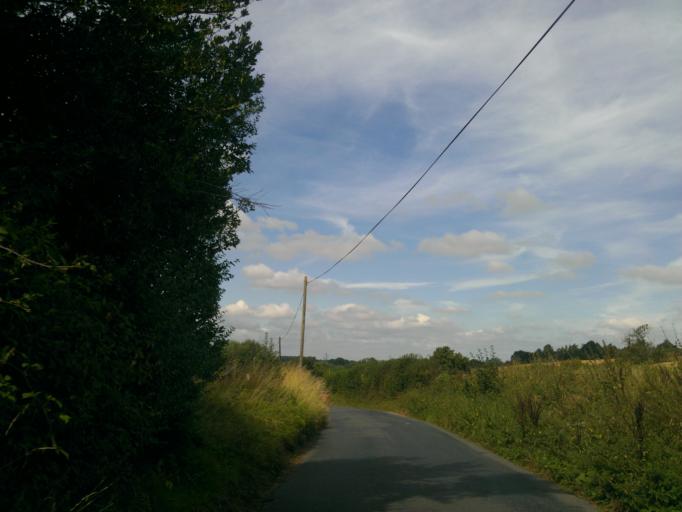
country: GB
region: England
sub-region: Essex
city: Sible Hedingham
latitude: 51.9811
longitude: 0.6041
